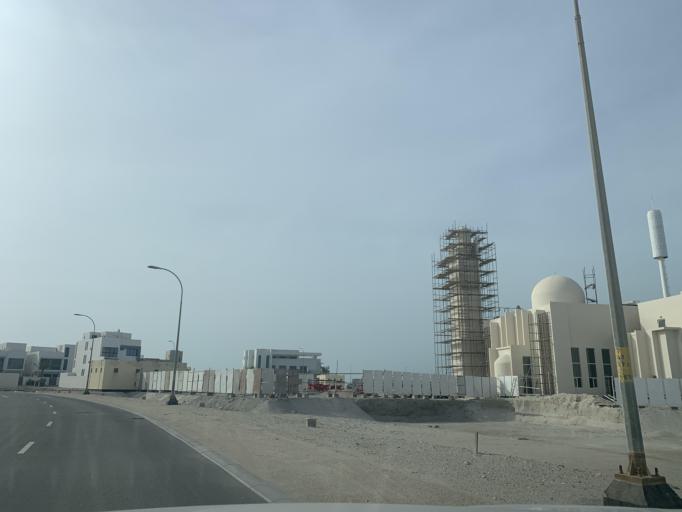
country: BH
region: Muharraq
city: Al Muharraq
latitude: 26.3218
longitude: 50.6256
